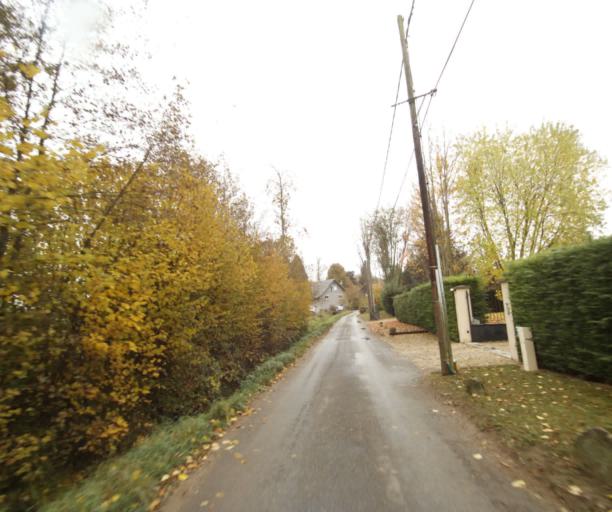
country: FR
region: Rhone-Alpes
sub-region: Departement de la Haute-Savoie
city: Reignier-Esery
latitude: 46.1277
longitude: 6.2995
